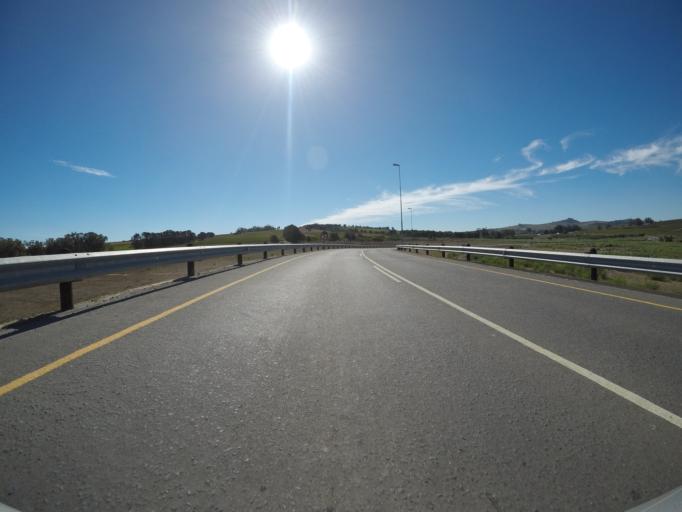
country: ZA
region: Western Cape
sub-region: Cape Winelands District Municipality
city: Stellenbosch
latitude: -33.9962
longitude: 18.7602
